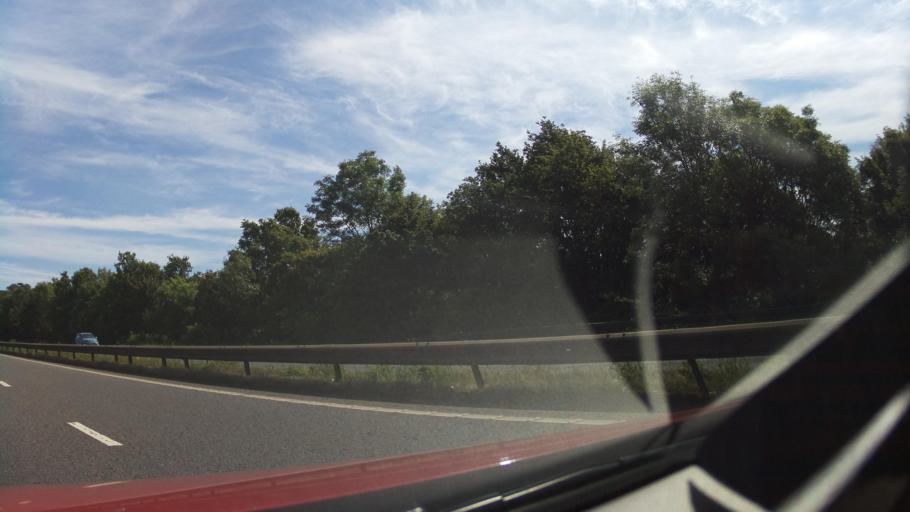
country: GB
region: England
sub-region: Lincolnshire
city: Burton
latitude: 53.2486
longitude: -0.5612
